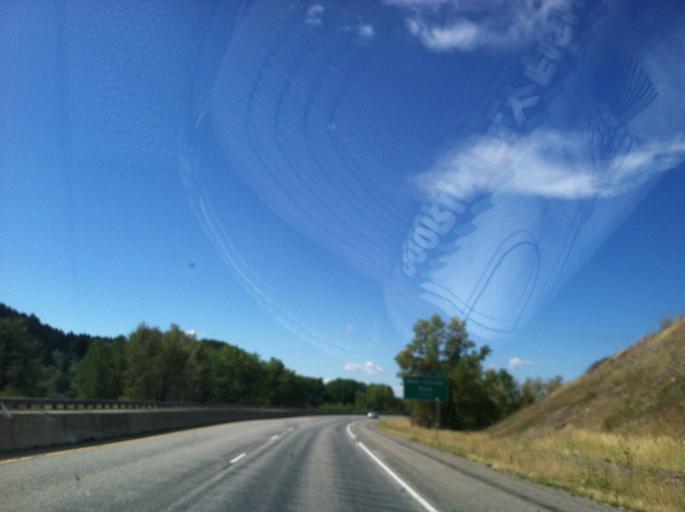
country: US
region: Montana
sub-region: Gallatin County
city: Bozeman
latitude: 45.6433
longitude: -110.9264
